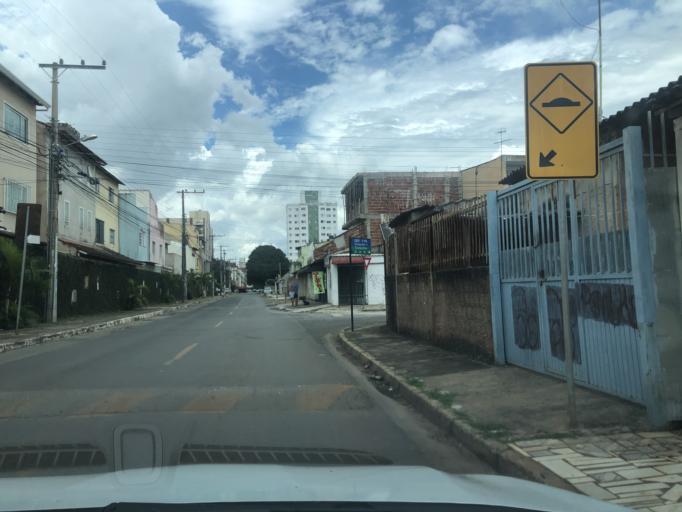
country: BR
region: Federal District
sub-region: Brasilia
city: Brasilia
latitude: -15.8693
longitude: -48.0678
